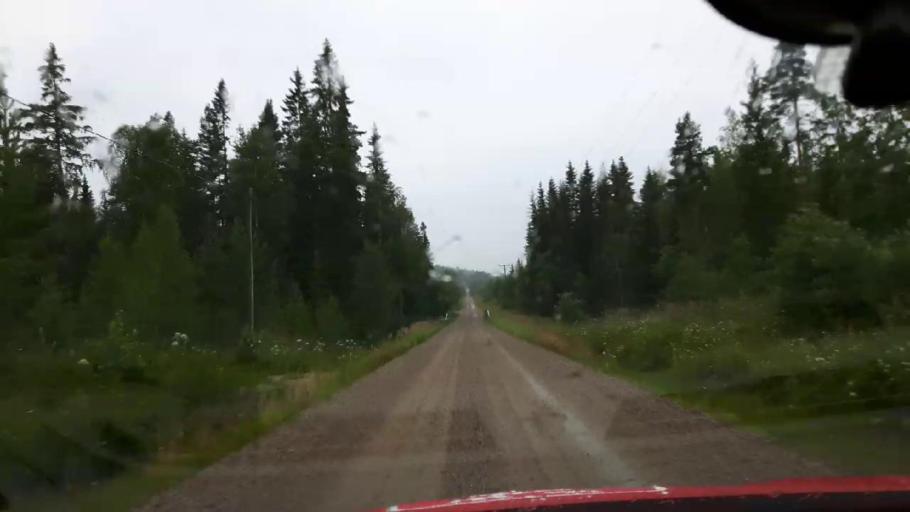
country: SE
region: Jaemtland
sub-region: OEstersunds Kommun
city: Brunflo
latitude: 62.7771
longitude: 14.9850
